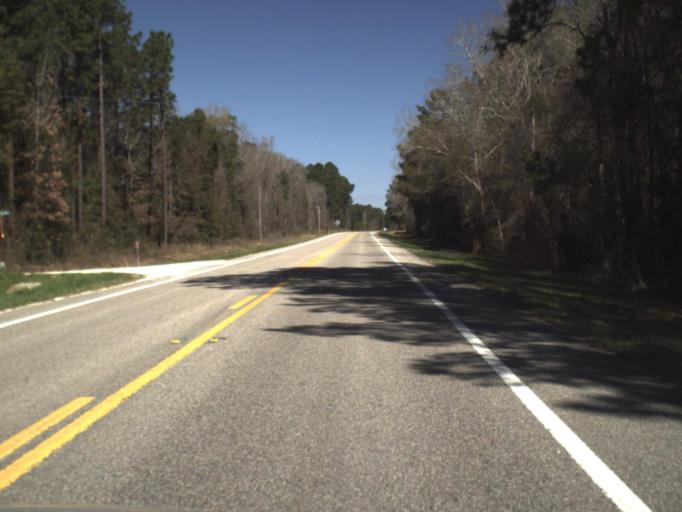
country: US
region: Florida
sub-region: Calhoun County
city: Blountstown
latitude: 30.5363
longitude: -85.0284
